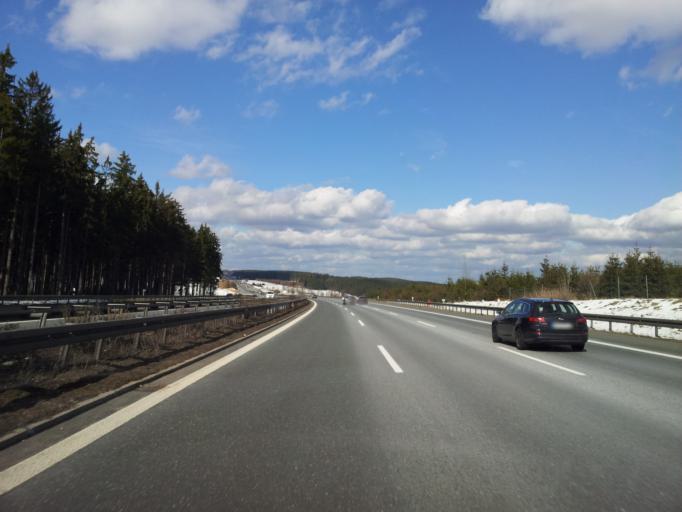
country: DE
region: Bavaria
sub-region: Upper Franconia
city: Leupoldsgrun
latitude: 50.2491
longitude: 11.7904
